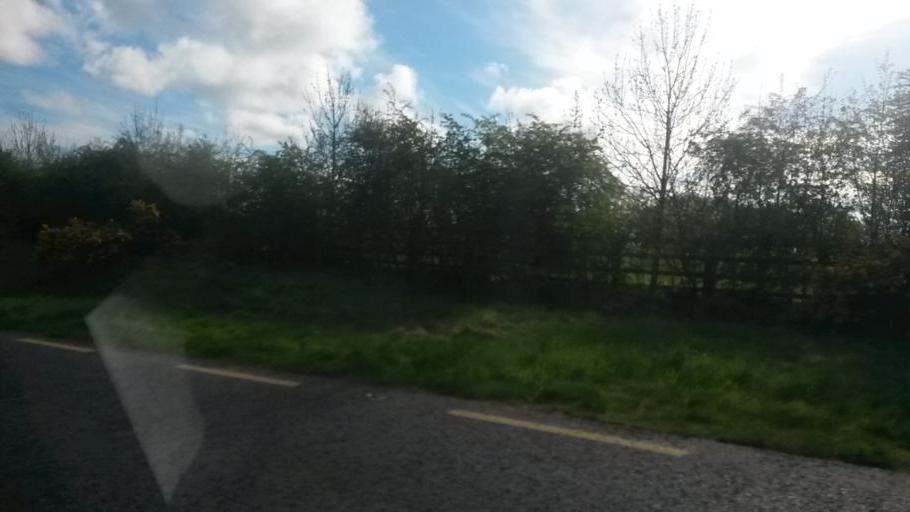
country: IE
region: Leinster
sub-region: An Mhi
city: Kells
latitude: 53.7155
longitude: -6.8486
